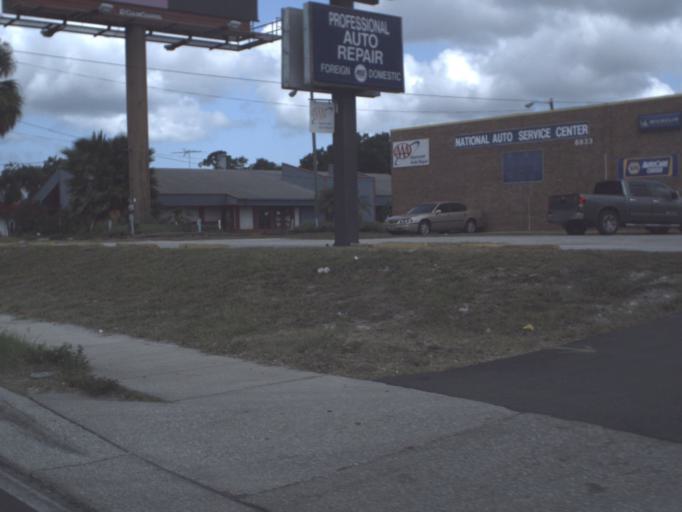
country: US
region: Florida
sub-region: Pasco County
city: Bayonet Point
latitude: 28.3313
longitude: -82.6684
